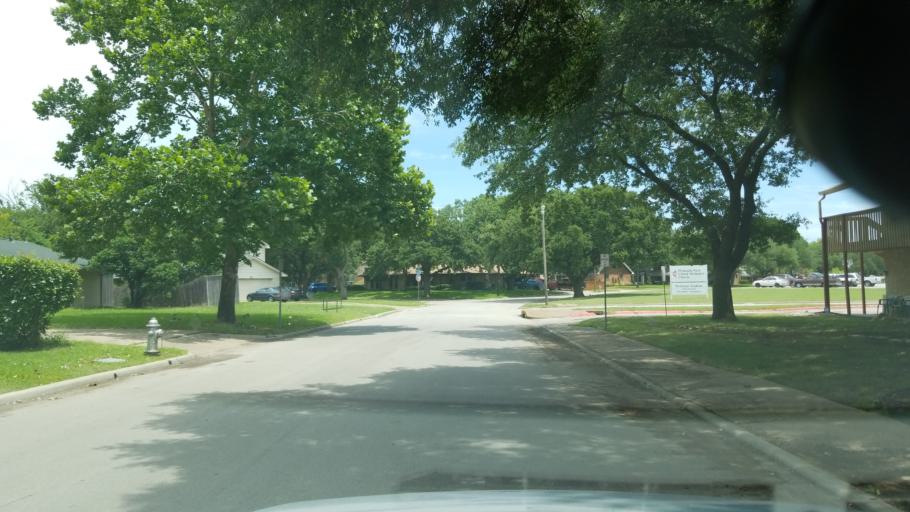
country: US
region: Texas
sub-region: Dallas County
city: Irving
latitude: 32.8389
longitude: -96.9684
